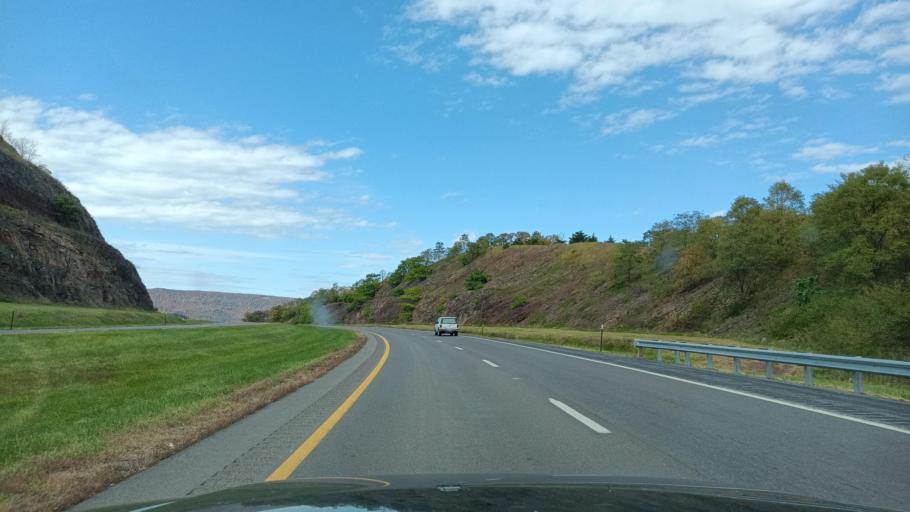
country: US
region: West Virginia
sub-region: Hardy County
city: Moorefield
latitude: 39.0917
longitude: -78.8046
